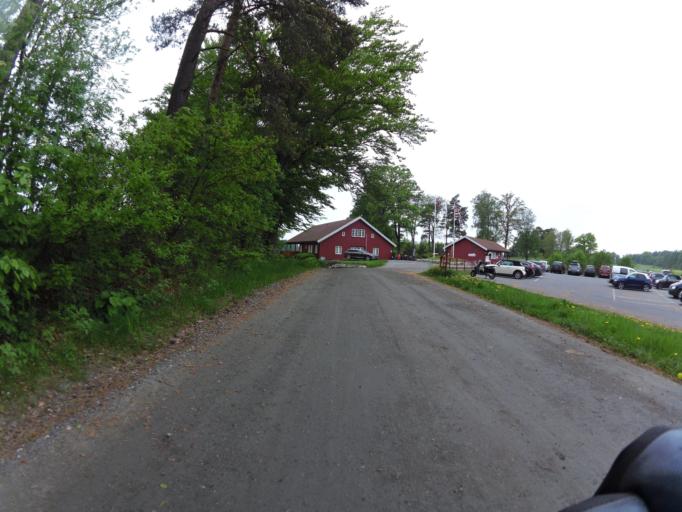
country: NO
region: Ostfold
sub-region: Rygge
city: Larkollen
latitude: 59.3683
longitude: 10.6820
